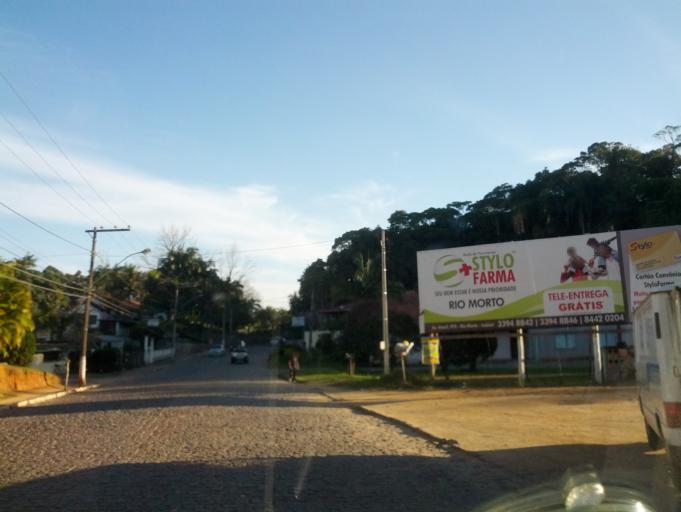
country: BR
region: Santa Catarina
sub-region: Indaial
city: Indaial
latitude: -26.8962
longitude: -49.2435
